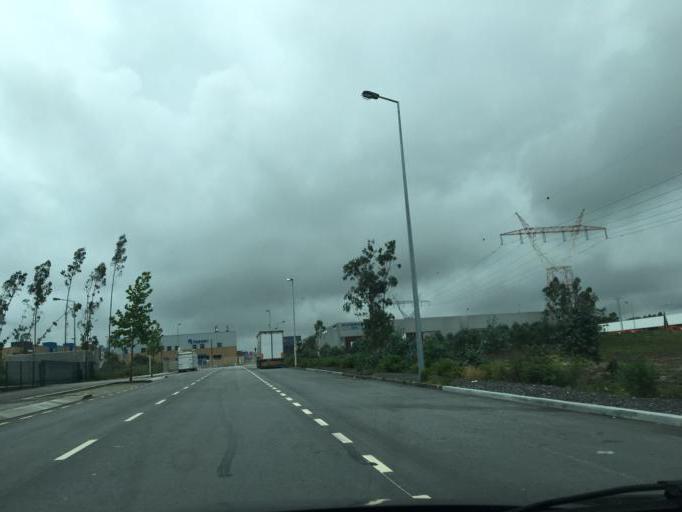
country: PT
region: Porto
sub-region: Maia
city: Maia
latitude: 41.2466
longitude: -8.6253
